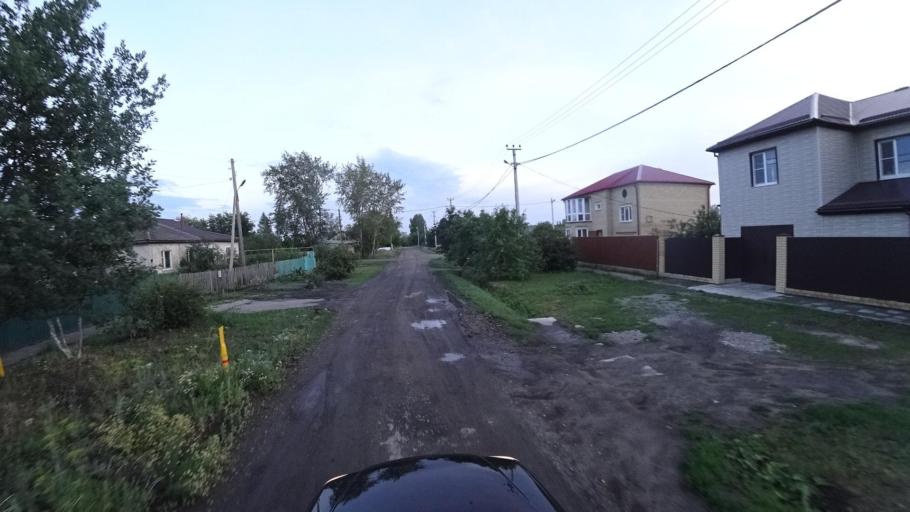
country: RU
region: Sverdlovsk
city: Kamyshlov
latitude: 56.8515
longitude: 62.7310
